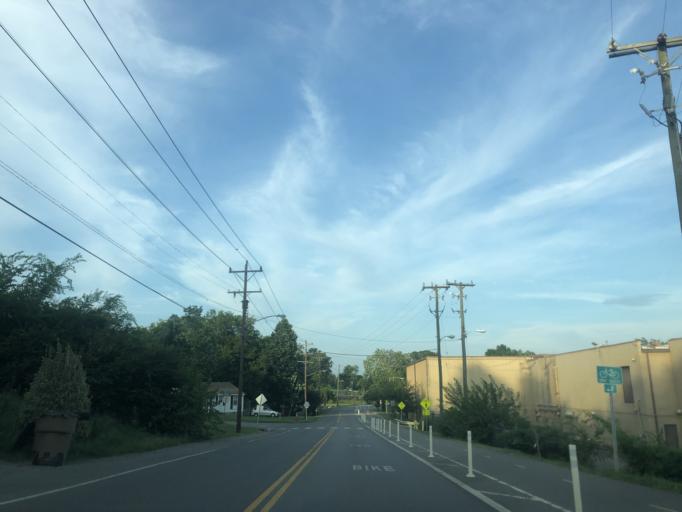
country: US
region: Tennessee
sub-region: Davidson County
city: Nashville
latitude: 36.1629
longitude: -86.7477
